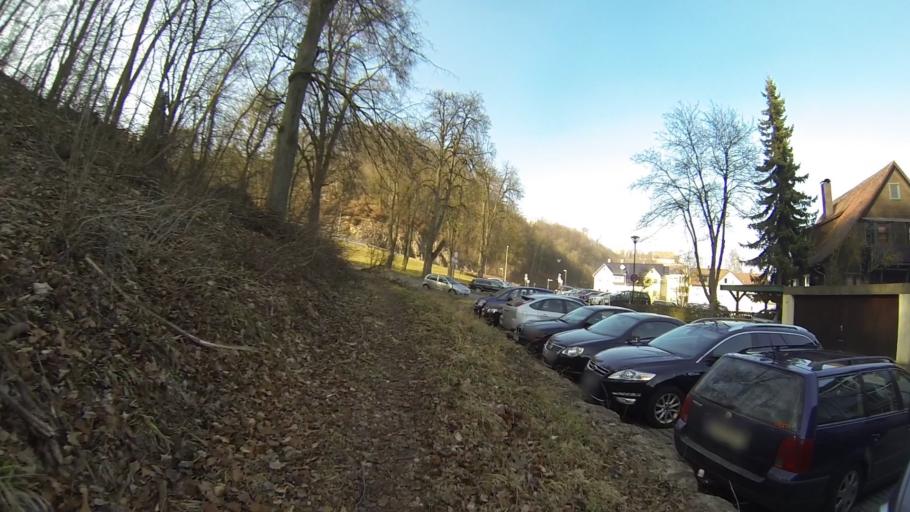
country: DE
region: Baden-Wuerttemberg
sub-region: Regierungsbezirk Stuttgart
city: Heidenheim an der Brenz
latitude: 48.6690
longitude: 10.1484
